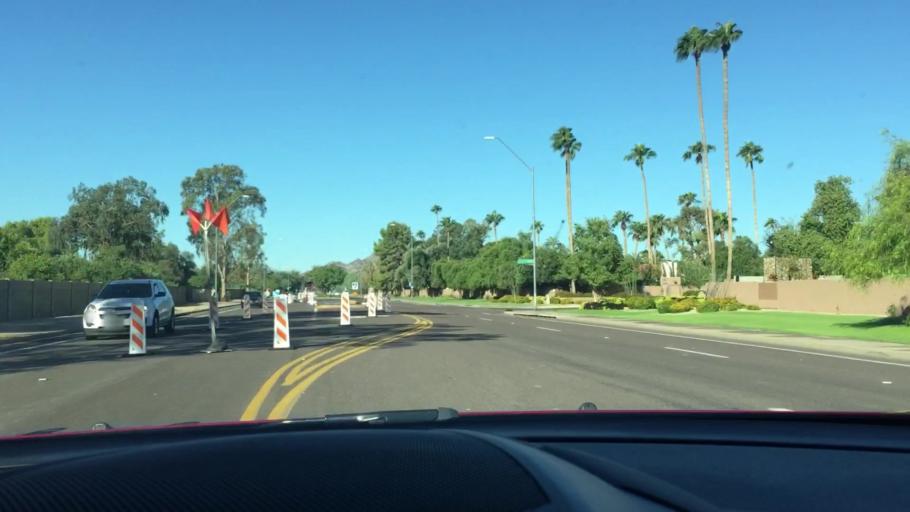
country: US
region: Arizona
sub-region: Maricopa County
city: Scottsdale
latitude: 33.5384
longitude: -111.8963
